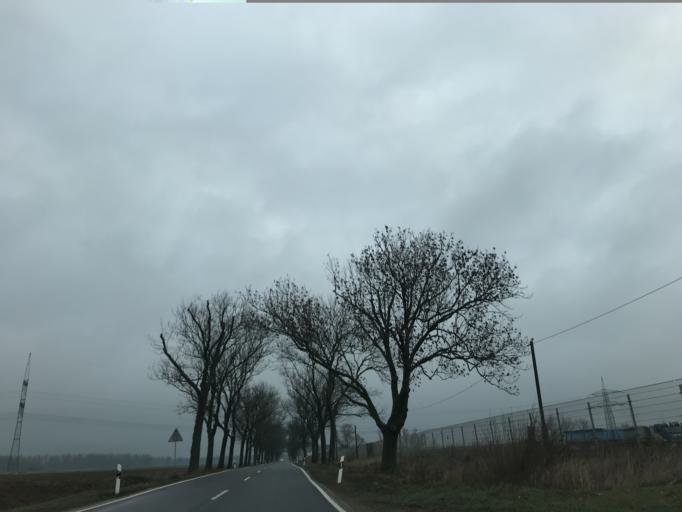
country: DE
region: Brandenburg
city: Wustermark
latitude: 52.5962
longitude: 12.9494
